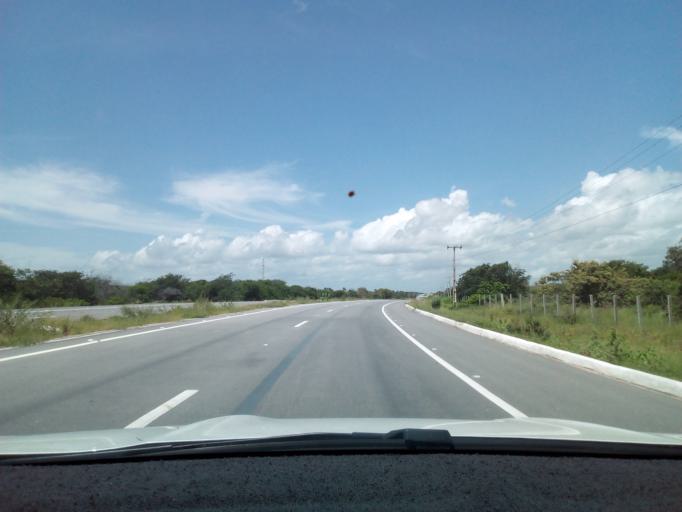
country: BR
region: Ceara
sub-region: Aracati
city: Aracati
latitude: -4.4627
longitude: -37.8016
